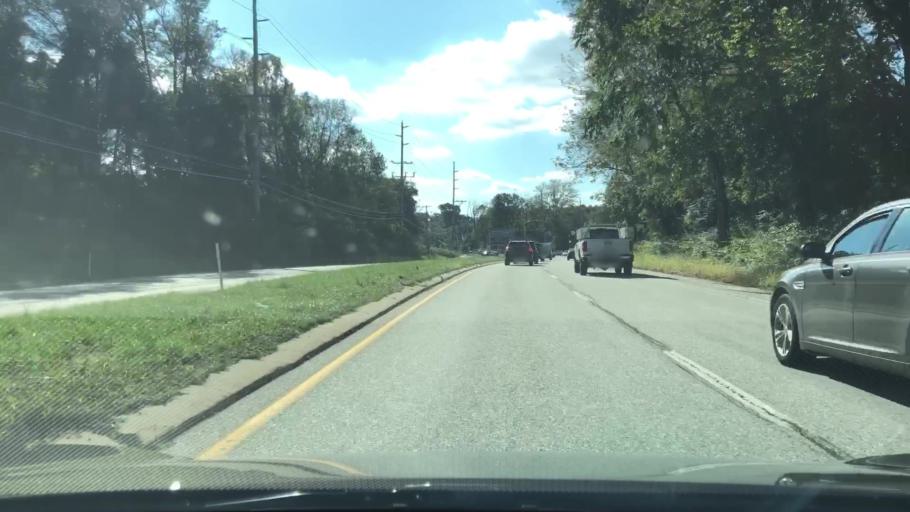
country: US
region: Pennsylvania
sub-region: Delaware County
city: Lima
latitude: 39.9655
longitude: -75.4867
